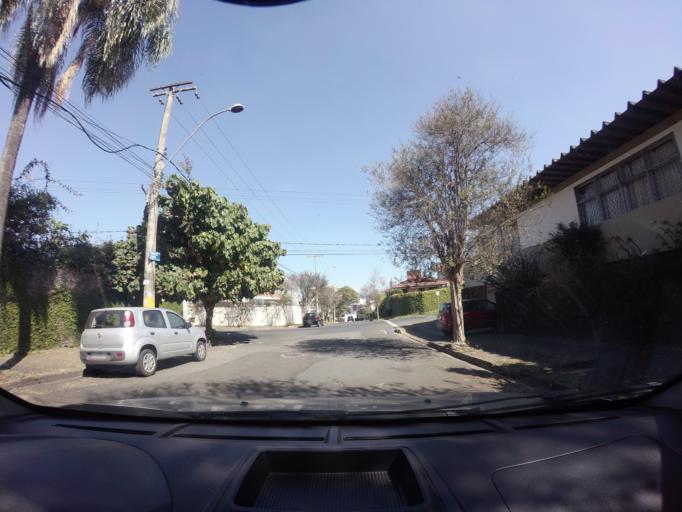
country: BR
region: Sao Paulo
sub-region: Piracicaba
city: Piracicaba
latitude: -22.7172
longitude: -47.6412
